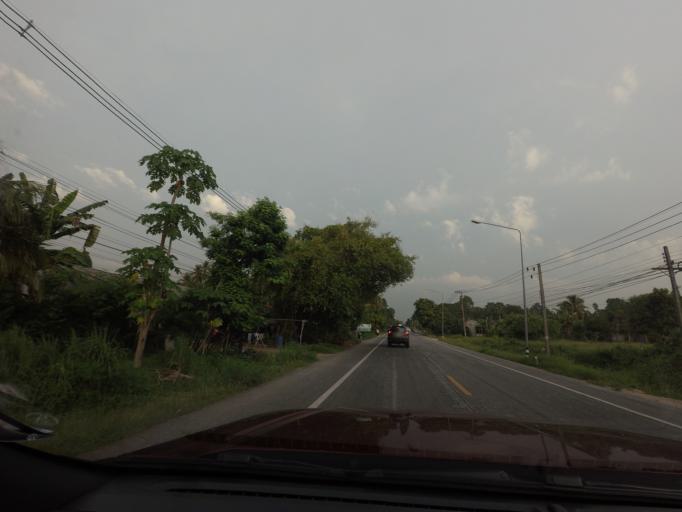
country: TH
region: Pattani
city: Mae Lan
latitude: 6.5986
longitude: 101.1944
